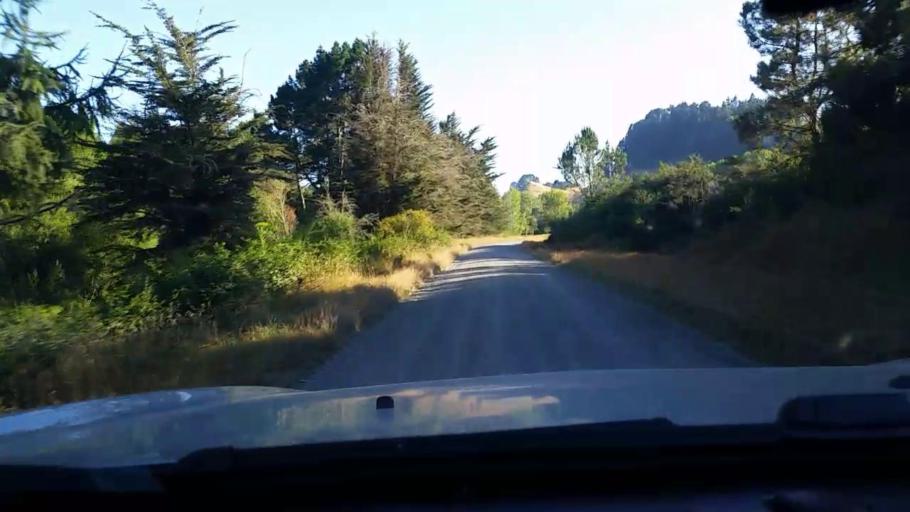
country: NZ
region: Waikato
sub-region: Taupo District
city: Taupo
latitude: -38.4597
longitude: 176.2410
